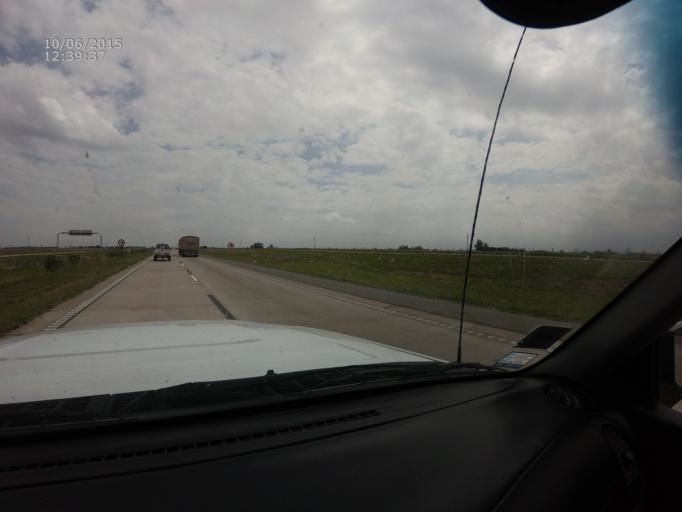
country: AR
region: Santa Fe
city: Carcarana
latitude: -32.8678
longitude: -61.2665
